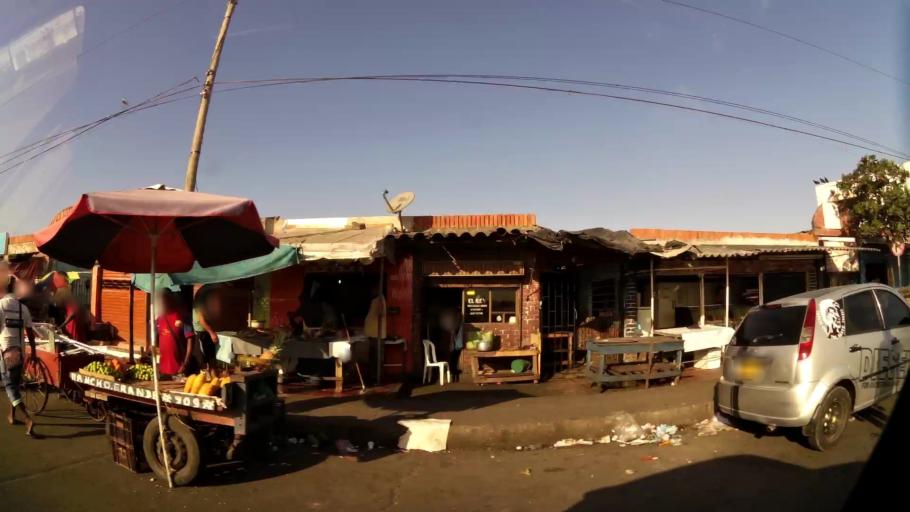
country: CO
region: Bolivar
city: Cartagena
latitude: 10.4120
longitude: -75.5259
